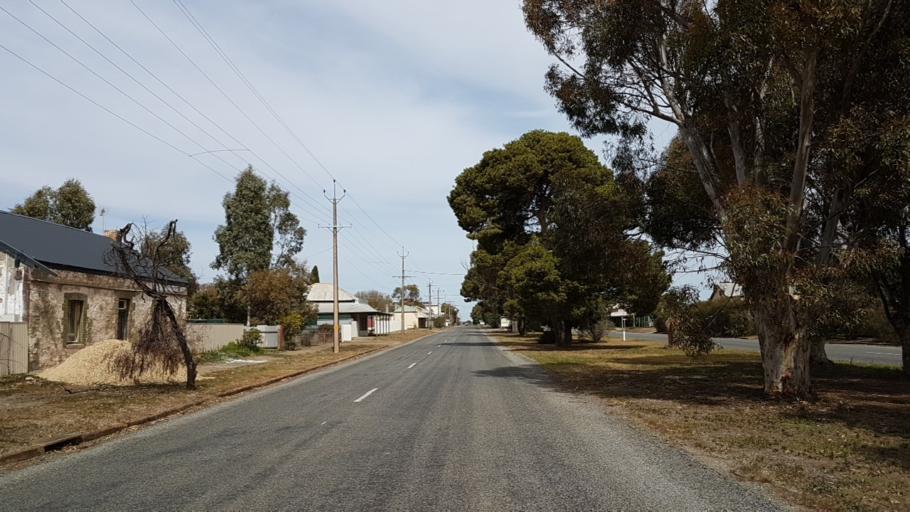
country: AU
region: South Australia
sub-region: Peterborough
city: Peterborough
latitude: -33.0269
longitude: 138.7500
